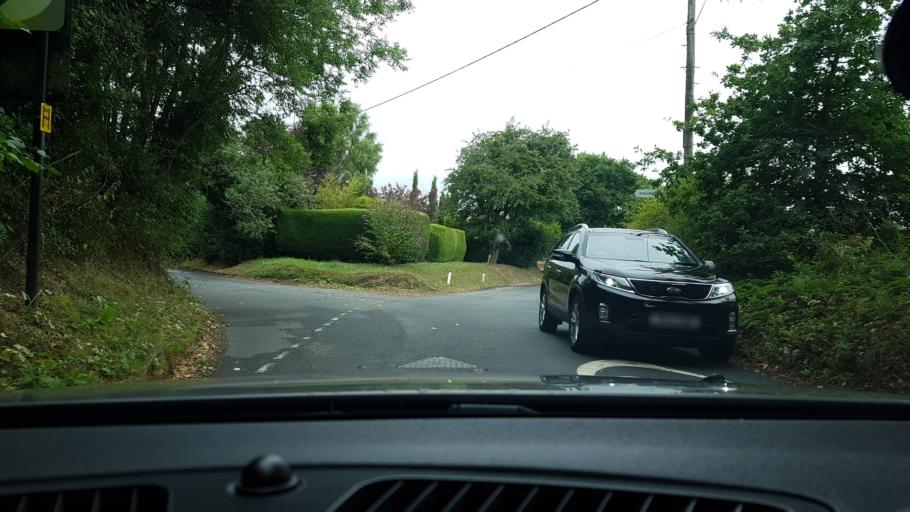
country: GB
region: England
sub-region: Wiltshire
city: Shalbourne
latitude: 51.3675
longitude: -1.5289
